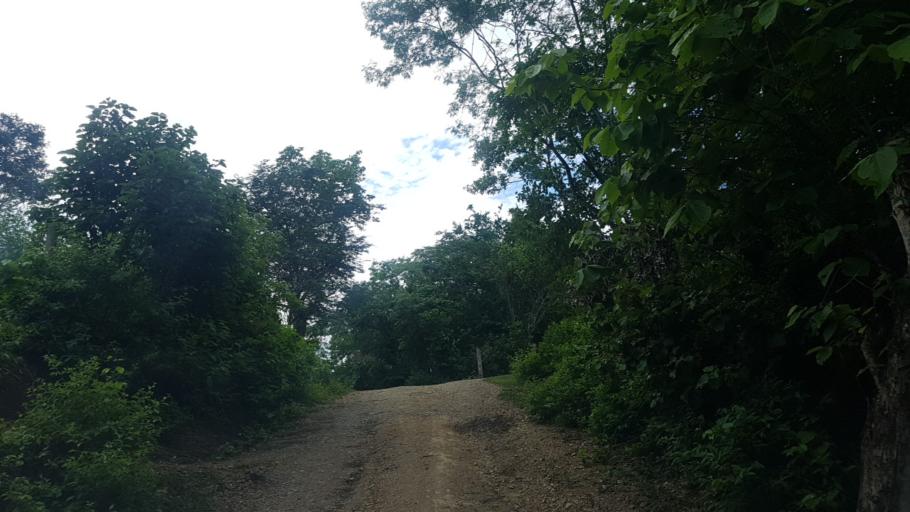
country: NI
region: Nueva Segovia
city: Ocotal
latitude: 13.5983
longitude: -86.4218
